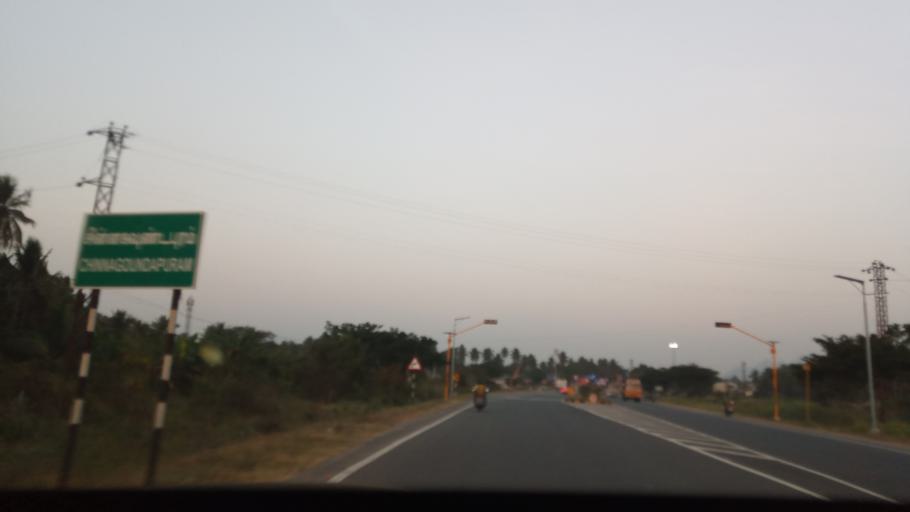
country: IN
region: Tamil Nadu
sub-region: Salem
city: Salem
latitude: 11.6660
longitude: 78.2526
